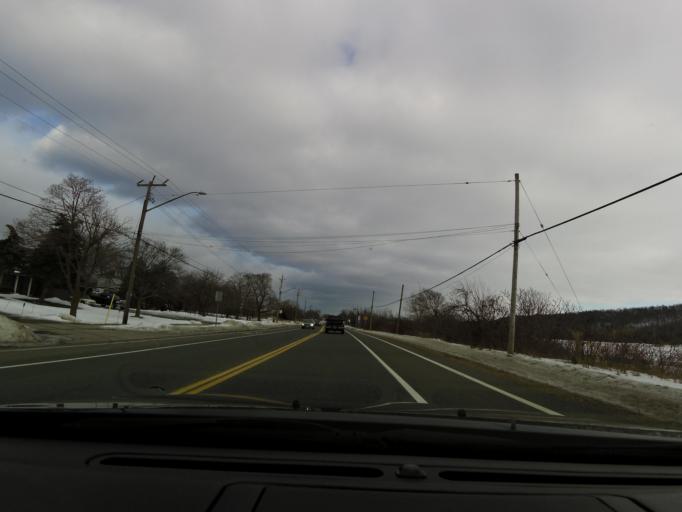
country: CA
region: Ontario
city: Hamilton
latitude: 43.2118
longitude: -79.6958
